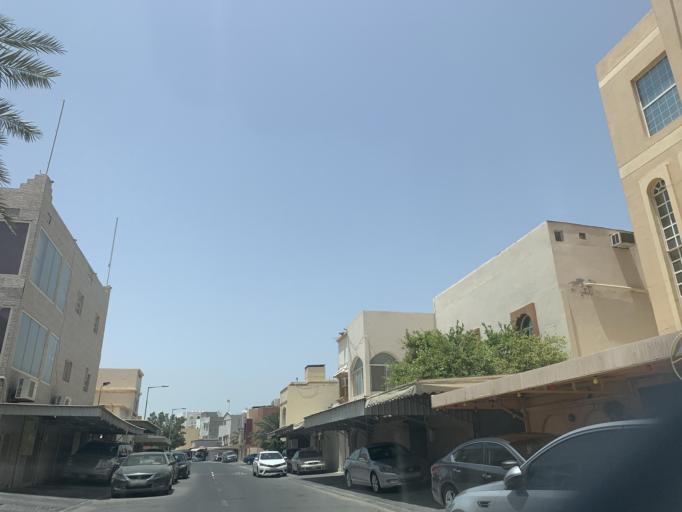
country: BH
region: Northern
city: Madinat `Isa
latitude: 26.1670
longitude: 50.5659
